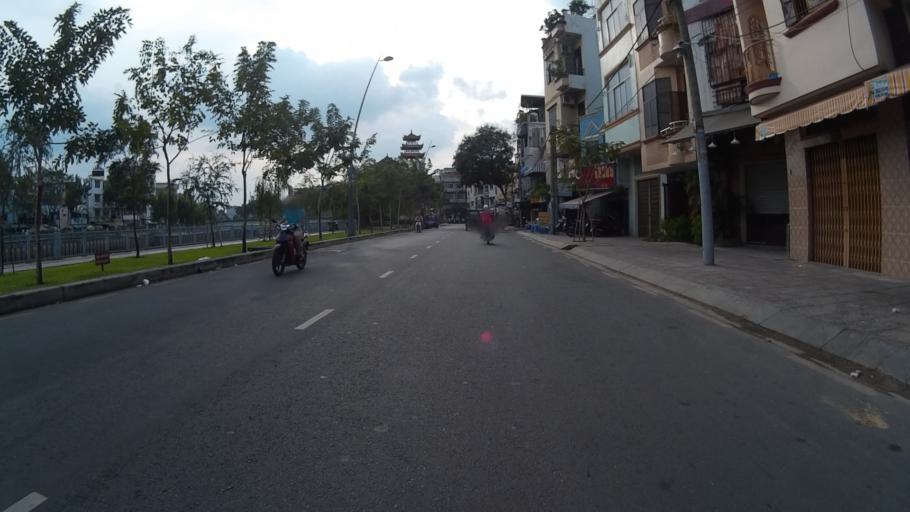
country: VN
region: Ho Chi Minh City
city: Quan Phu Nhuan
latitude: 10.7869
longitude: 106.6827
